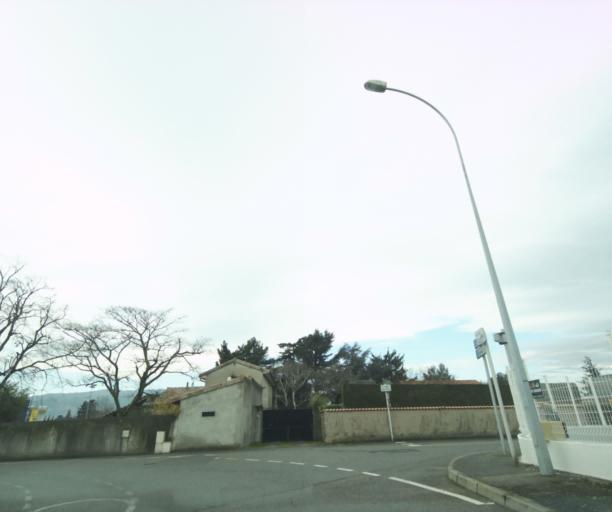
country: FR
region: Rhone-Alpes
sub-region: Departement de la Drome
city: Bourg-les-Valence
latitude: 44.9613
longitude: 4.8836
